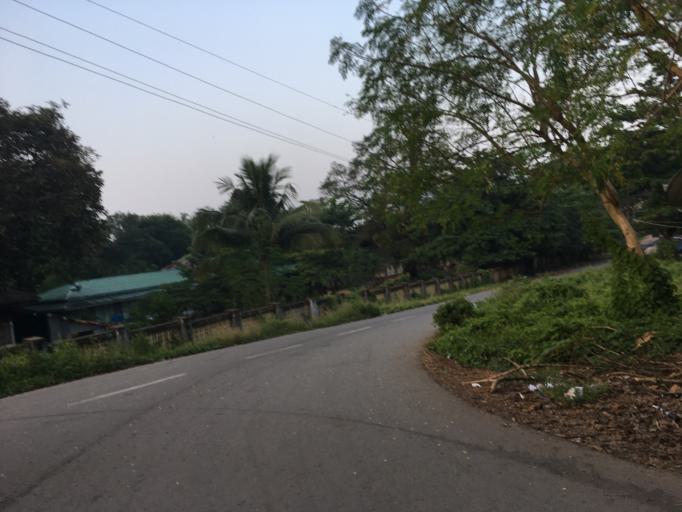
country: MM
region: Mon
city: Mawlamyine
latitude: 16.4805
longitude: 97.6263
